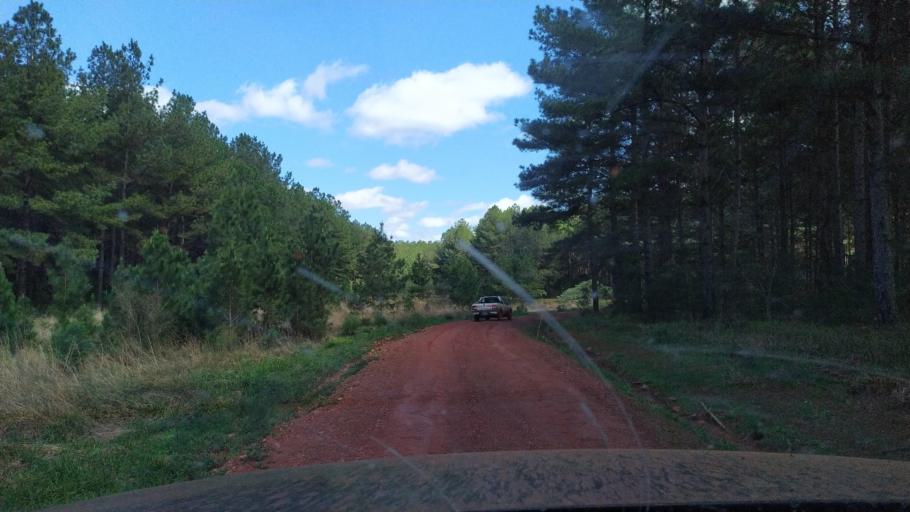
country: AR
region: Corrientes
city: Santo Tome
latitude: -28.4644
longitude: -55.9909
